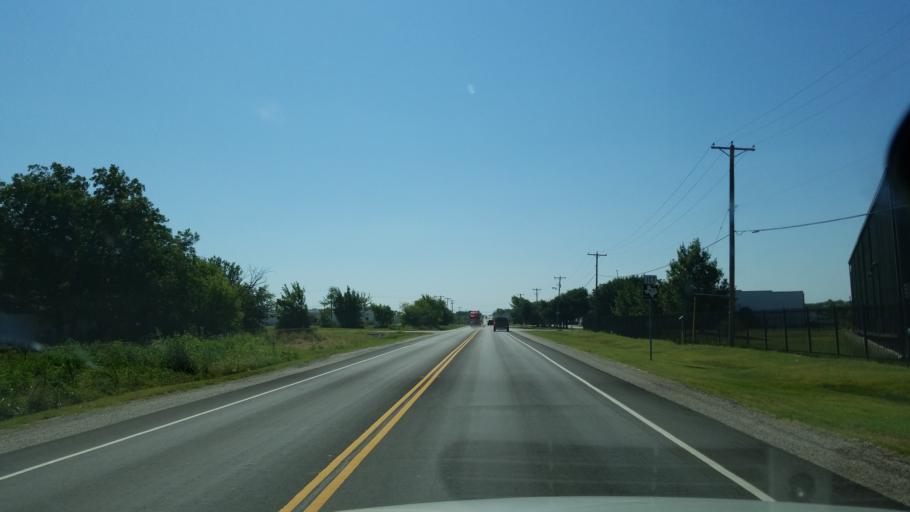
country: US
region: Texas
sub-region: Tarrant County
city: Mansfield
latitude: 32.5522
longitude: -97.1340
